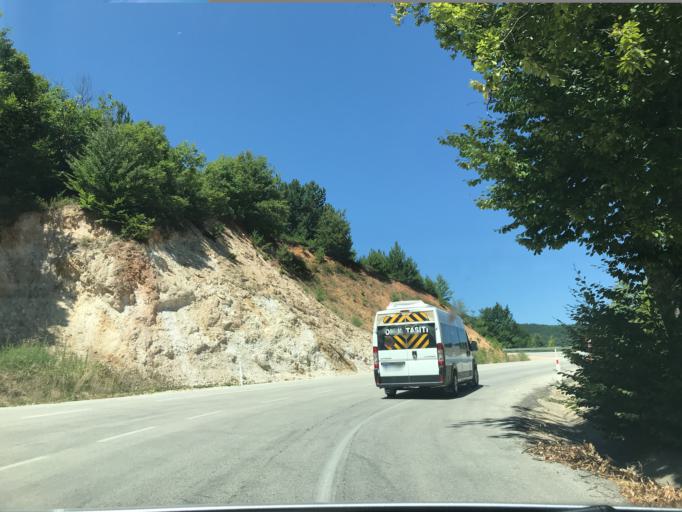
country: TR
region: Bursa
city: Tahtakopru
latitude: 39.9422
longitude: 29.6000
